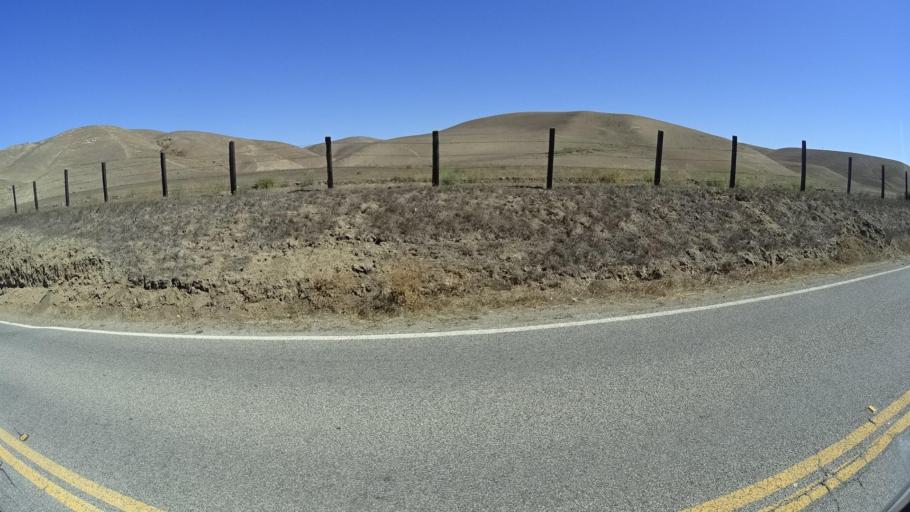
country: US
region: California
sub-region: Monterey County
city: Greenfield
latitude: 36.3140
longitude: -121.1721
